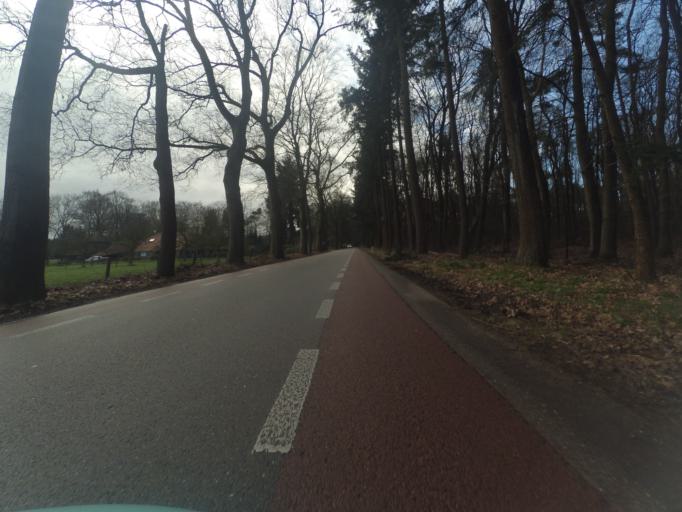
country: NL
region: Gelderland
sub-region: Gemeente Apeldoorn
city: Beekbergen
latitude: 52.1098
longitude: 5.8764
